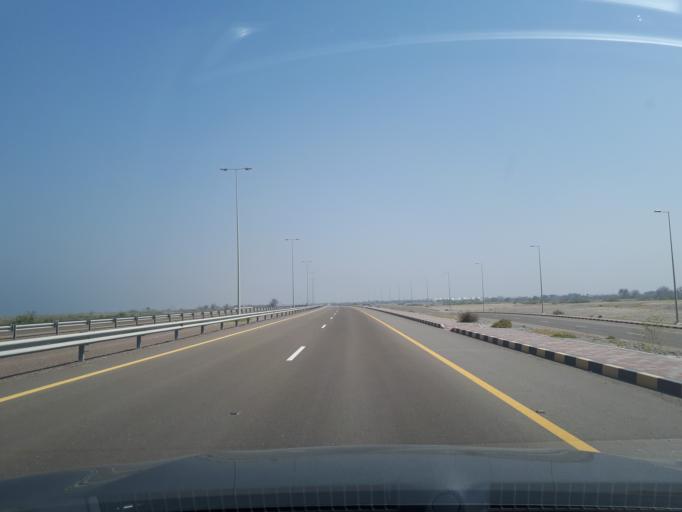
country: AE
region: Al Fujayrah
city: Al Fujayrah
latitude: 24.9300
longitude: 56.3839
